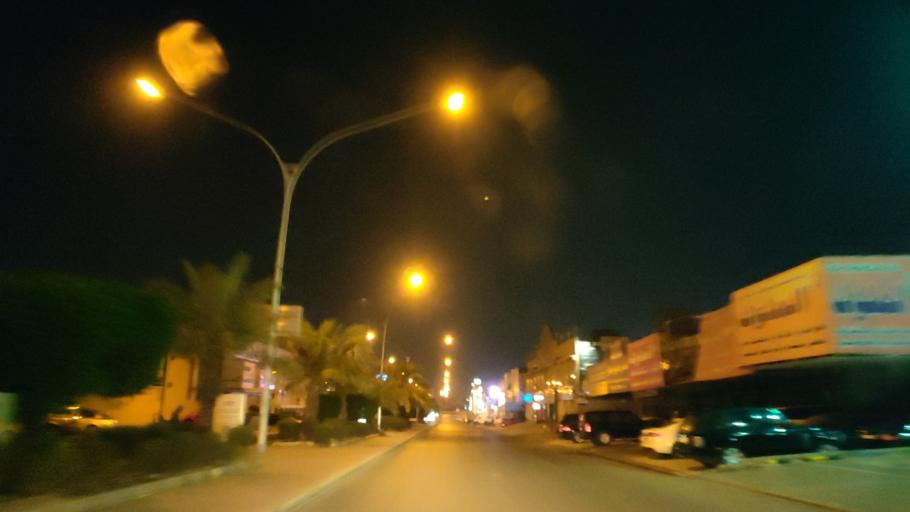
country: KW
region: Al Asimah
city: Ar Rabiyah
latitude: 29.3095
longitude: 47.9352
